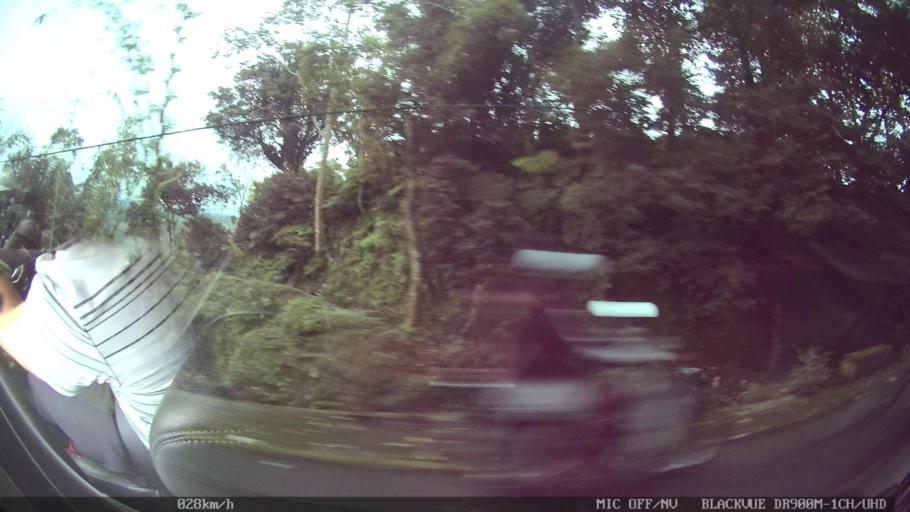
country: ID
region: Bali
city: Peneng
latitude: -8.3250
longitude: 115.1982
